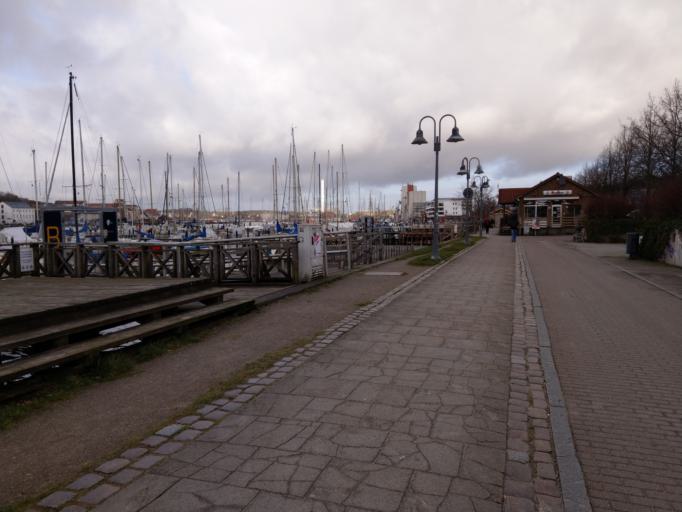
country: DE
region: Schleswig-Holstein
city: Flensburg
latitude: 54.7895
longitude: 9.4376
